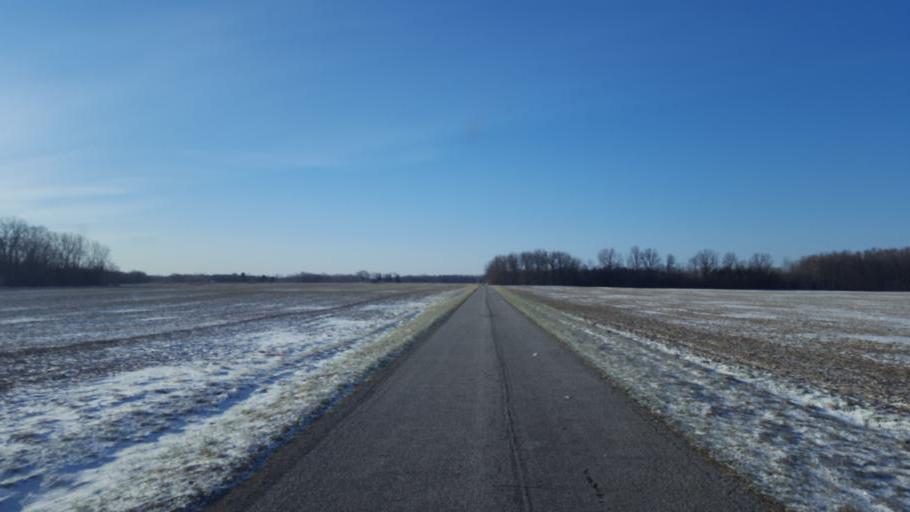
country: US
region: Ohio
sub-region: Morrow County
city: Mount Gilead
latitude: 40.6126
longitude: -82.8852
